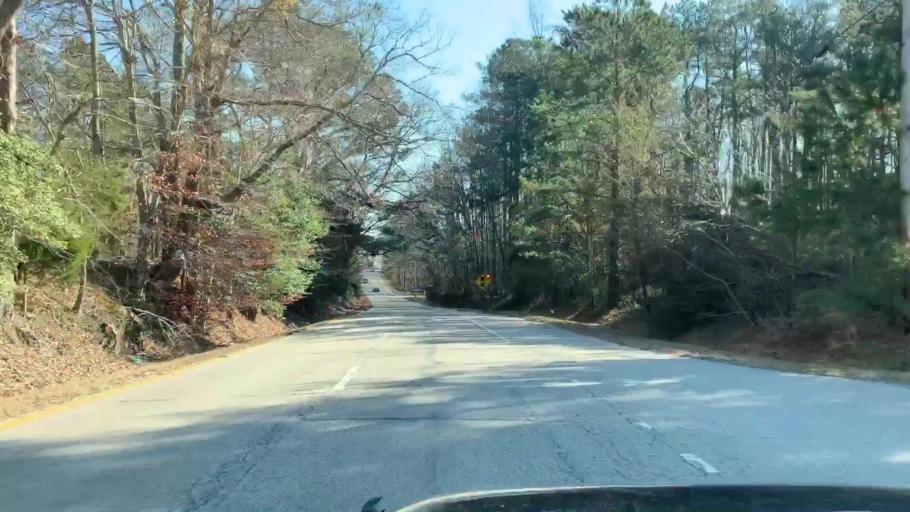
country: US
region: Virginia
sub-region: James City County
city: Williamsburg
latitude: 37.3743
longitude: -76.7822
